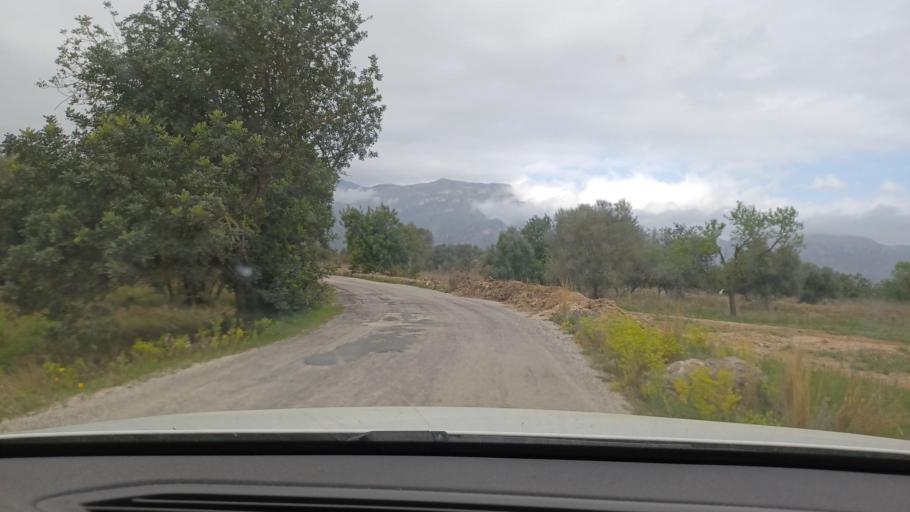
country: ES
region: Catalonia
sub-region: Provincia de Tarragona
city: Tortosa
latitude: 40.7952
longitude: 0.4500
